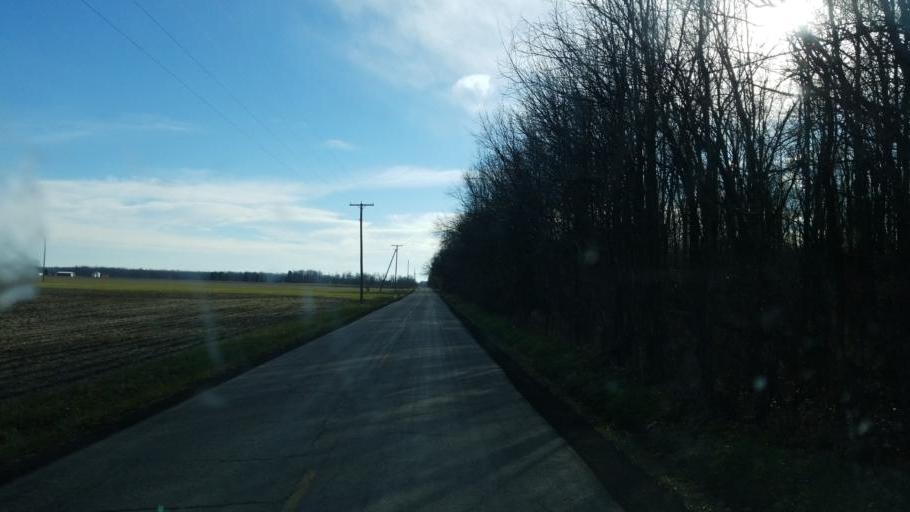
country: US
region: Ohio
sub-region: Crawford County
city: Crestline
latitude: 40.8089
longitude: -82.6972
